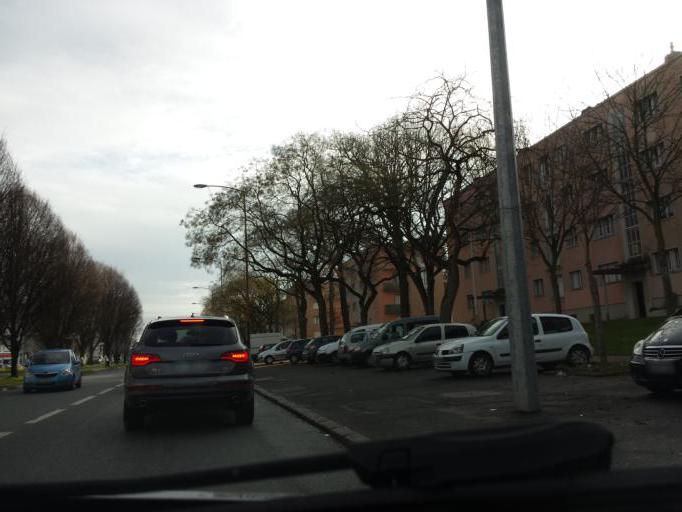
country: FR
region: Ile-de-France
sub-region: Departement des Hauts-de-Seine
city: Chatenay-Malabry
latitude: 48.7681
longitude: 2.2519
